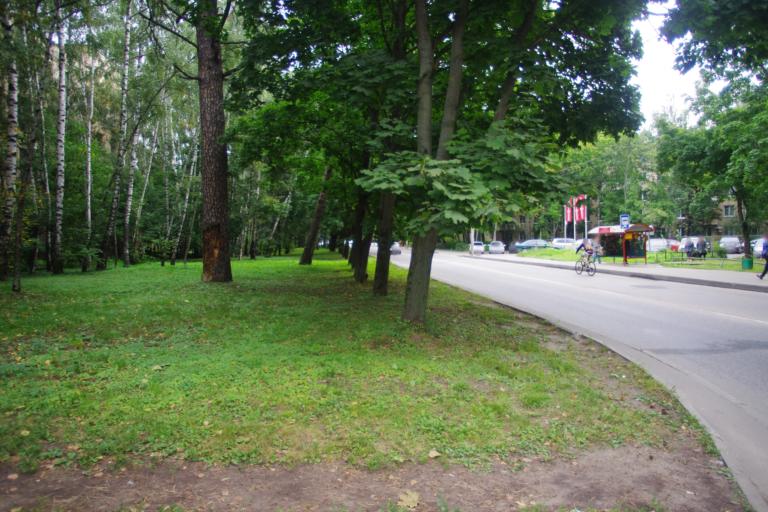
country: RU
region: Moskovskaya
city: Krasnogorsk
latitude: 55.8182
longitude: 37.3208
